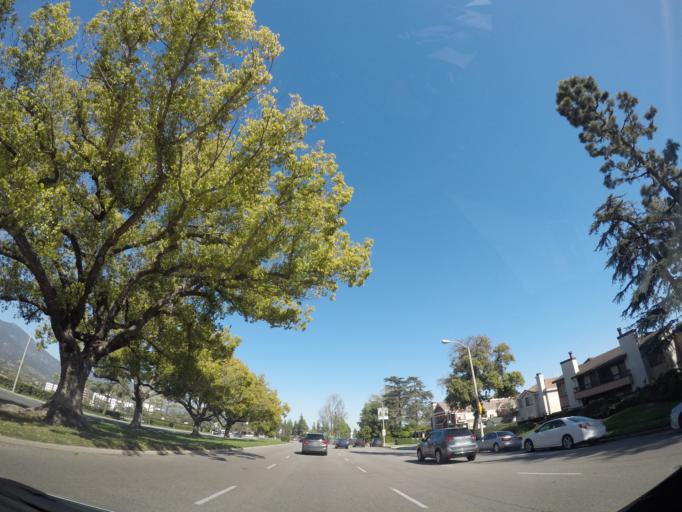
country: US
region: California
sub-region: Los Angeles County
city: Arcadia
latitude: 34.1315
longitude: -118.0480
